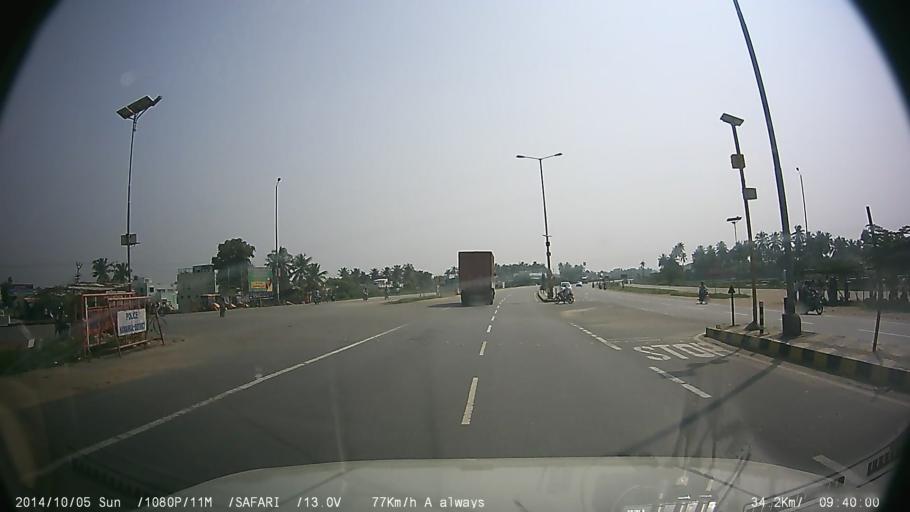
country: IN
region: Tamil Nadu
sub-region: Erode
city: Bhavani
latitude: 11.4436
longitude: 77.7146
